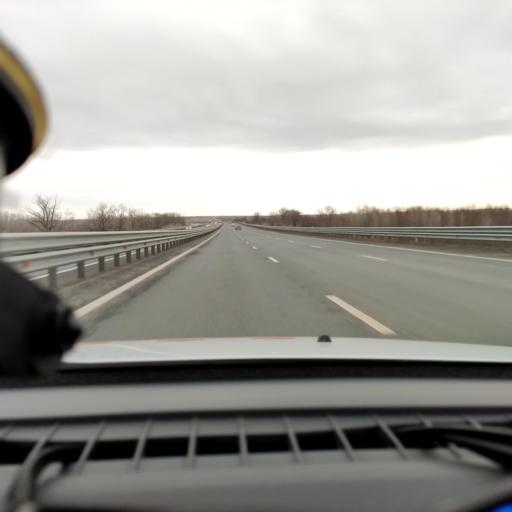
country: RU
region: Samara
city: Smyshlyayevka
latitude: 53.1735
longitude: 50.3125
